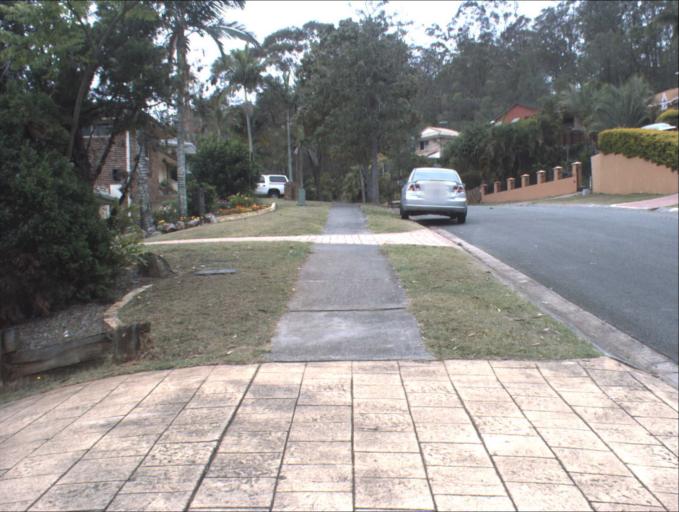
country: AU
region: Queensland
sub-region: Logan
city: Slacks Creek
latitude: -27.6754
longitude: 153.1697
